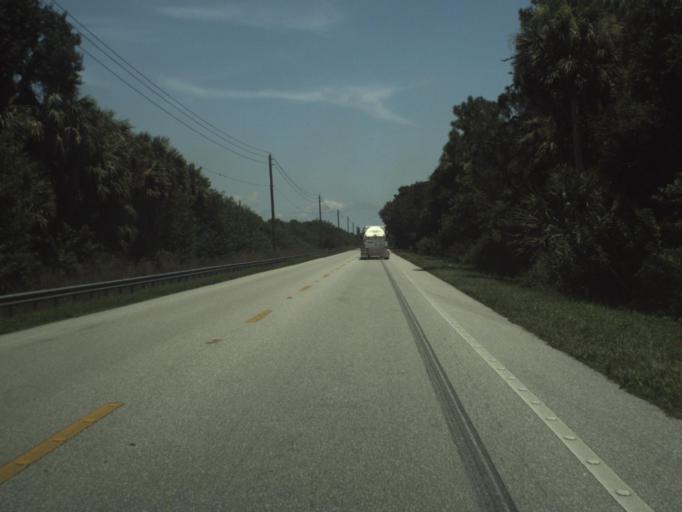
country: US
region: Florida
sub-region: Martin County
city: Indiantown
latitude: 27.0907
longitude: -80.5743
